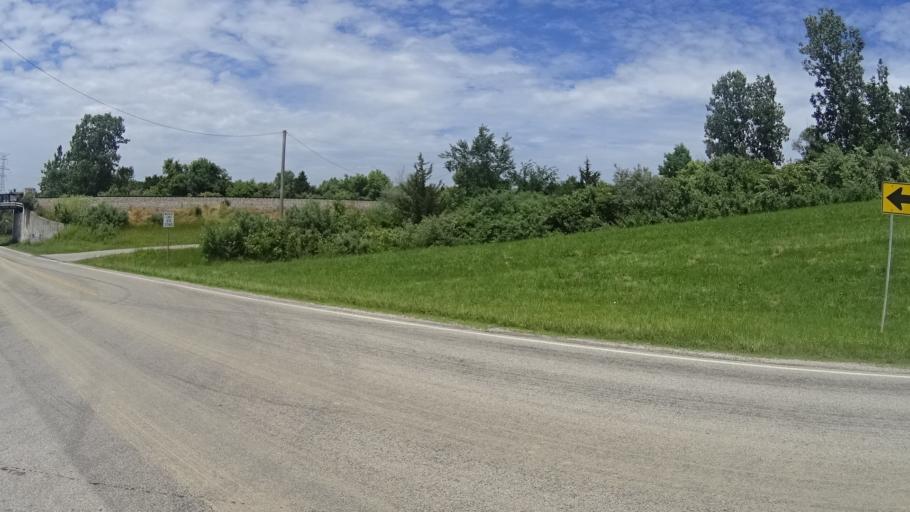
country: US
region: Ohio
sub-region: Erie County
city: Milan
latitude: 41.3337
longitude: -82.5710
